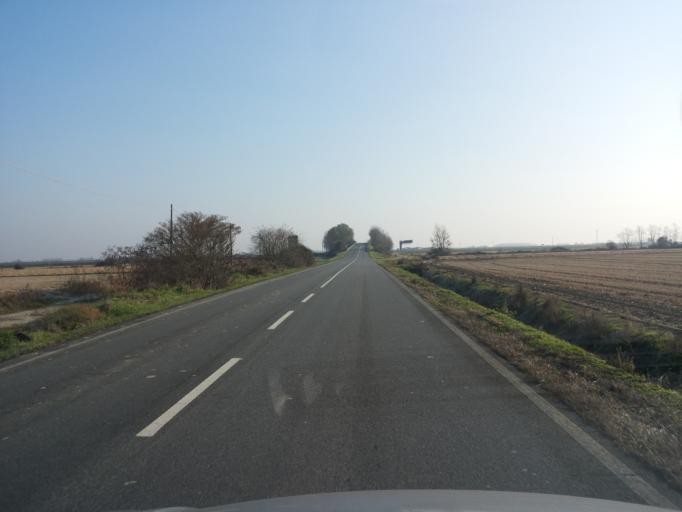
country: IT
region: Piedmont
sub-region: Provincia di Vercelli
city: Stroppiana
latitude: 45.2268
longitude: 8.4707
